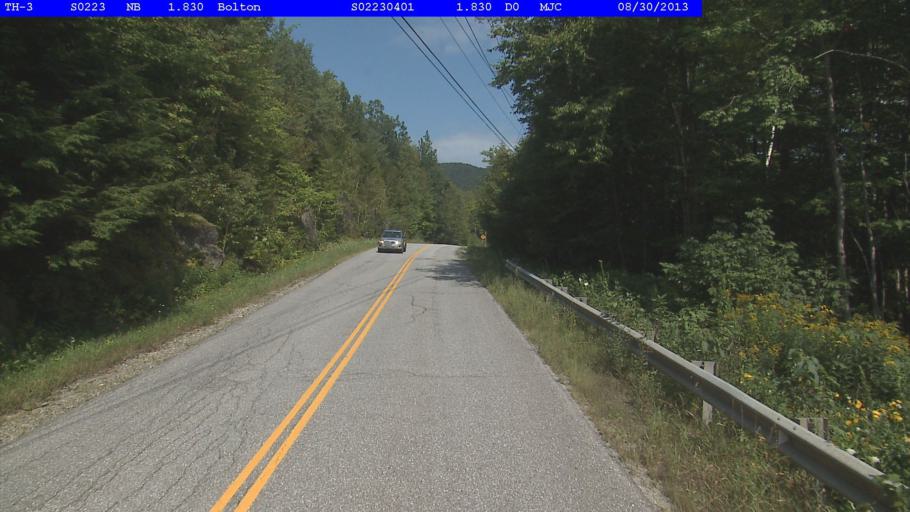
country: US
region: Vermont
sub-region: Washington County
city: Waterbury
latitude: 44.3961
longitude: -72.8779
